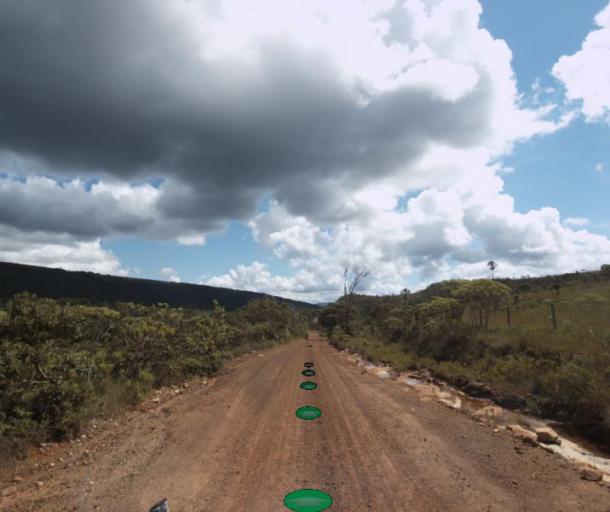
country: BR
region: Goias
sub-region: Pirenopolis
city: Pirenopolis
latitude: -15.7874
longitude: -48.8683
